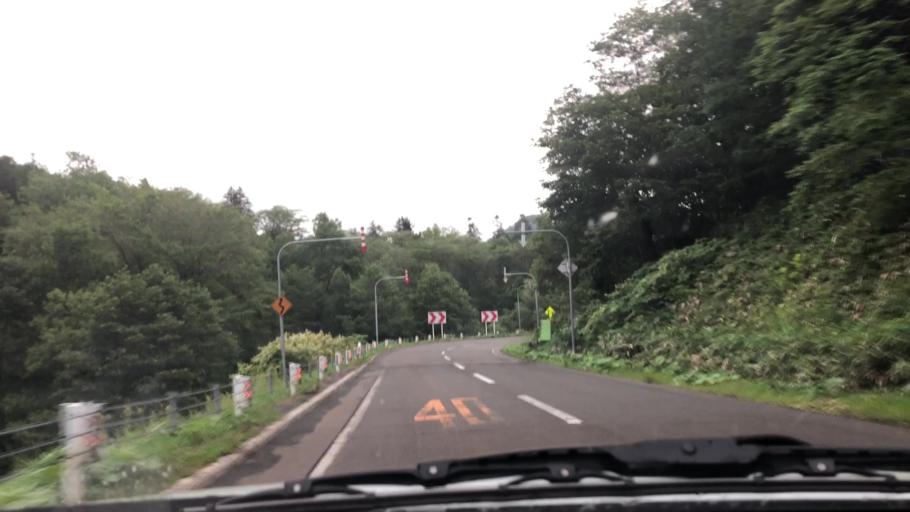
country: JP
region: Hokkaido
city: Shimo-furano
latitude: 42.9300
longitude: 142.3742
